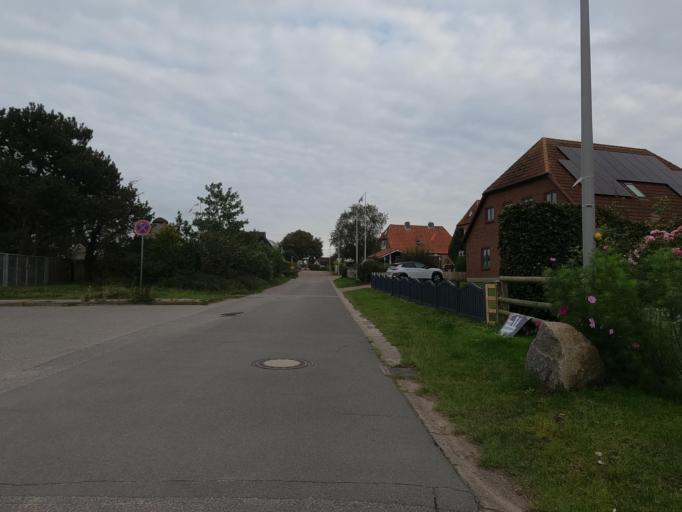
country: DE
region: Schleswig-Holstein
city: Heiligenhafen
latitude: 54.3674
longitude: 11.0198
